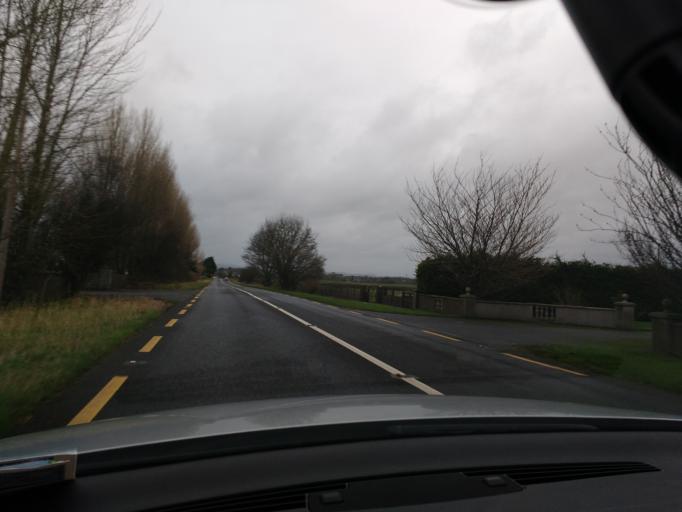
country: IE
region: Munster
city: Thurles
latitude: 52.6736
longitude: -7.7605
